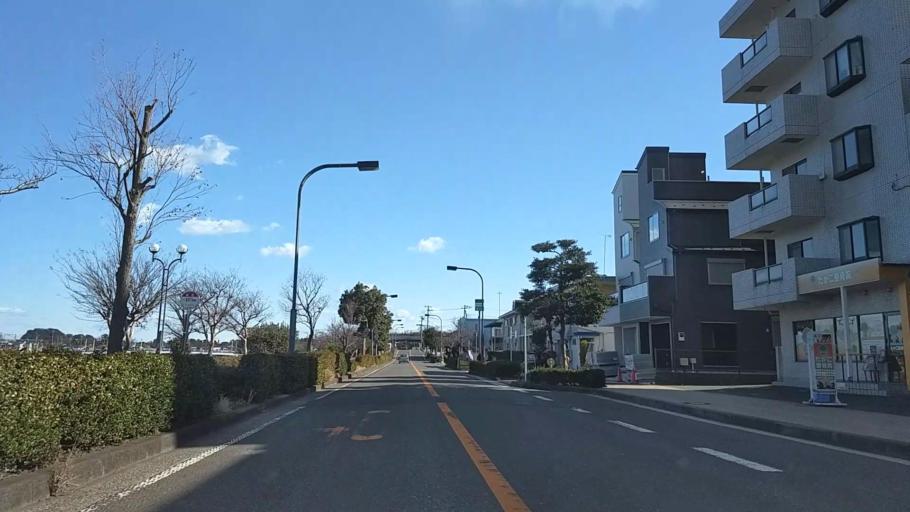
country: JP
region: Kanagawa
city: Yokosuka
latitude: 35.3274
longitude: 139.6272
